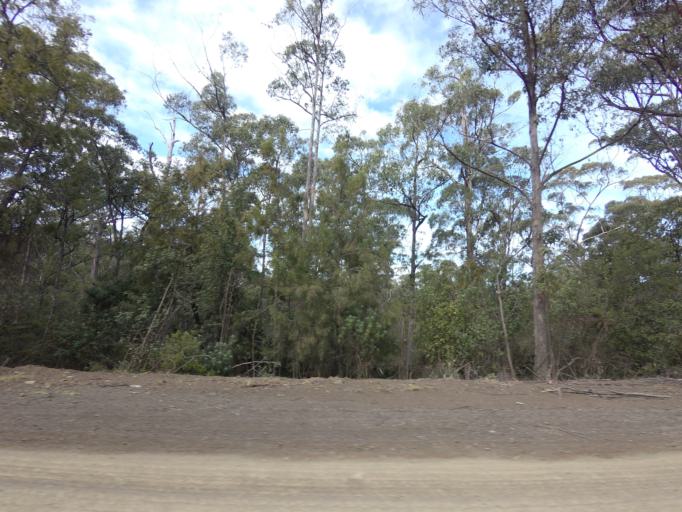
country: AU
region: Tasmania
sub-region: Clarence
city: Sandford
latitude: -43.0875
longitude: 147.7111
